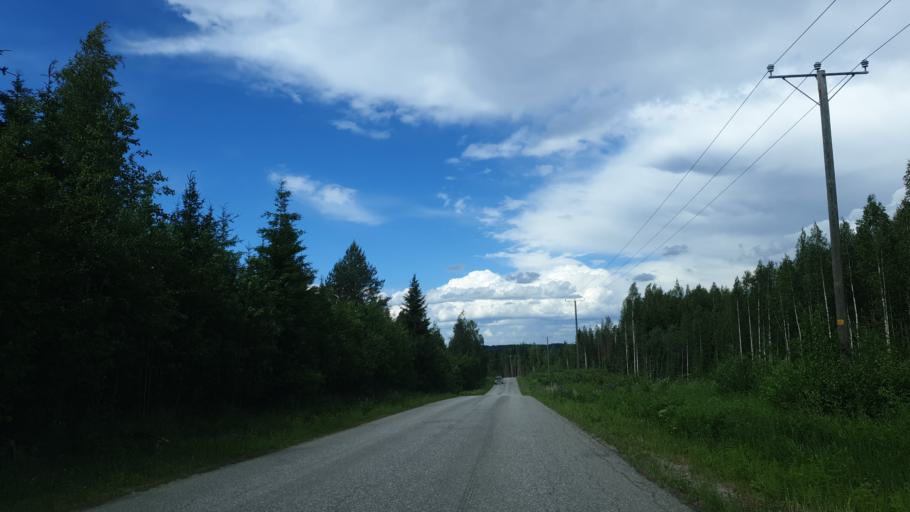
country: FI
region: Northern Savo
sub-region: Koillis-Savo
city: Kaavi
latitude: 62.9781
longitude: 28.7471
